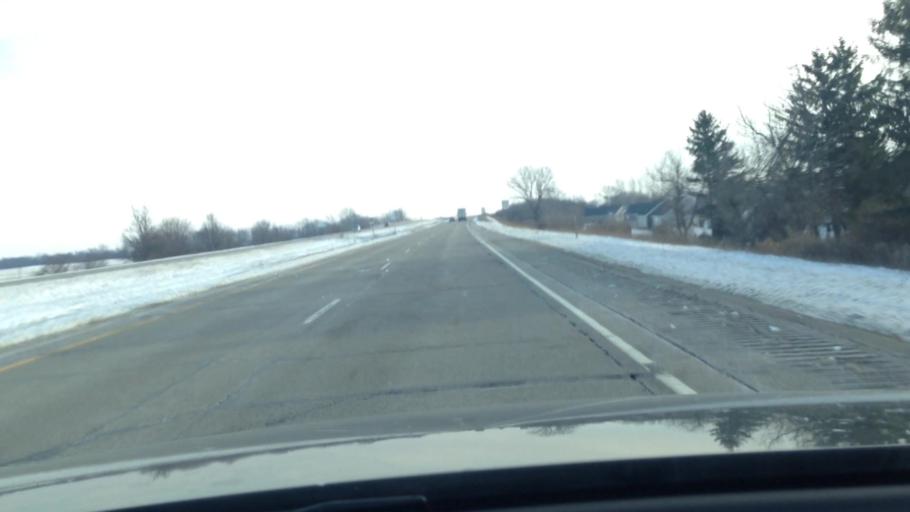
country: US
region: Wisconsin
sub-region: Walworth County
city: Elkhorn
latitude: 42.6610
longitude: -88.5125
